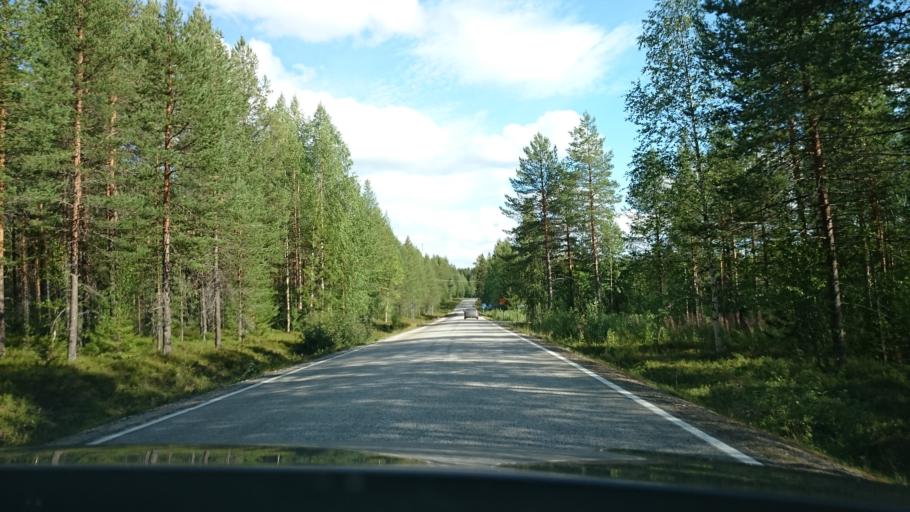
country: FI
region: Kainuu
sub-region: Kehys-Kainuu
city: Suomussalmi
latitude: 64.7496
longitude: 29.4302
